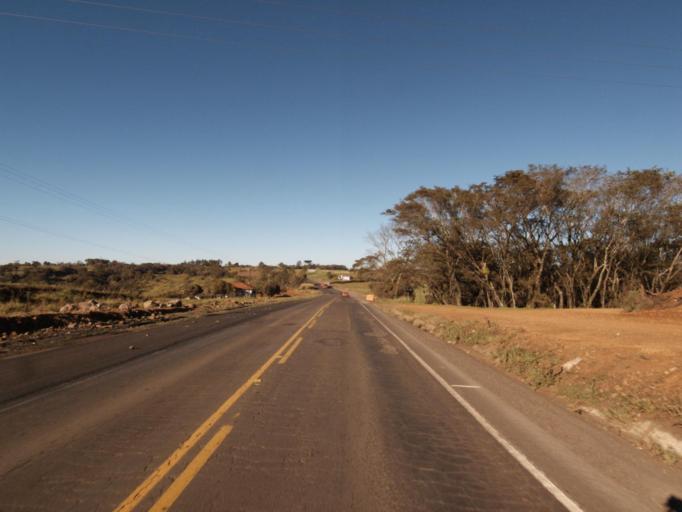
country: AR
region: Misiones
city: Bernardo de Irigoyen
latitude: -26.6436
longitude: -53.5188
